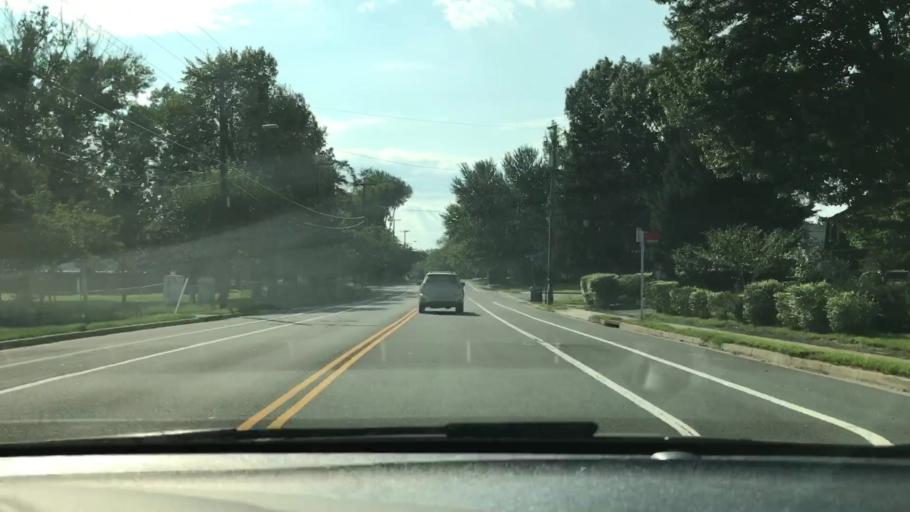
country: US
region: Virginia
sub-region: Fairfax County
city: Jefferson
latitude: 38.8576
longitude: -77.1814
